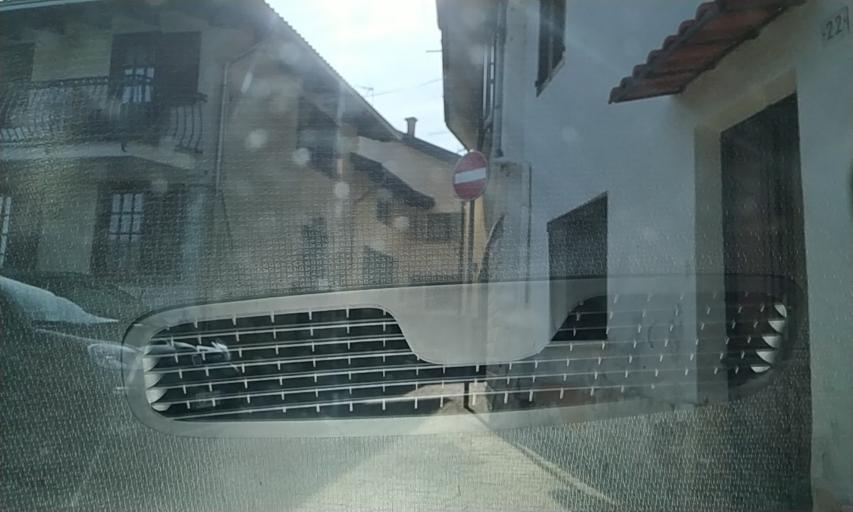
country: IT
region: Piedmont
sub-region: Provincia di Biella
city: Portula
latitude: 45.6806
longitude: 8.1760
